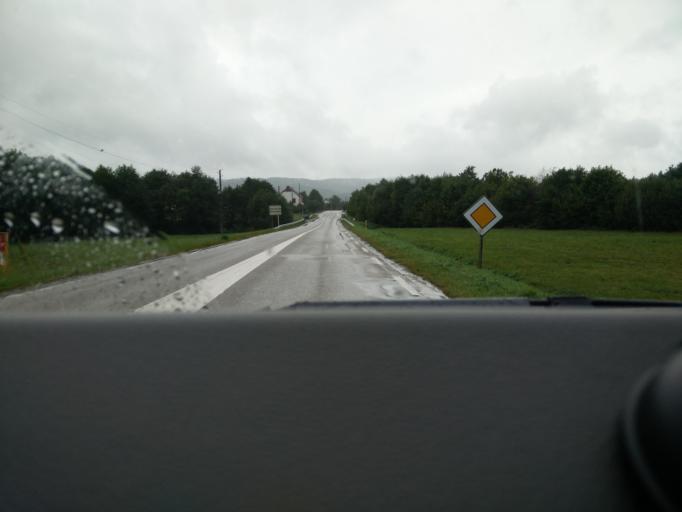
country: FR
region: Lorraine
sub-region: Departement des Vosges
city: Fraize
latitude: 48.1837
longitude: 6.9723
